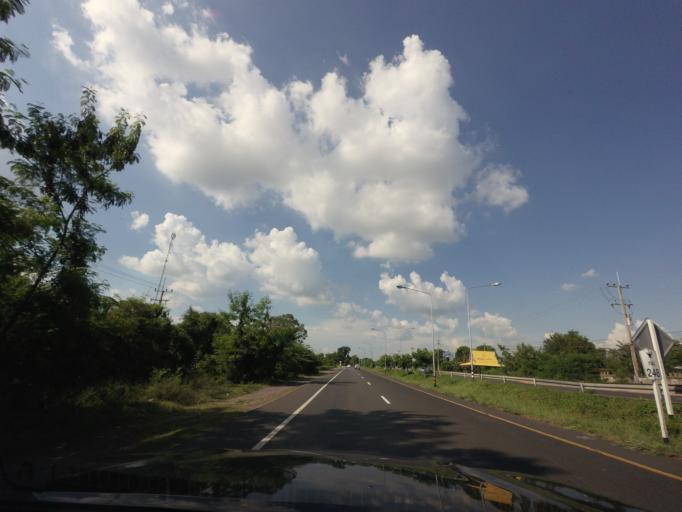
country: TH
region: Nakhon Ratchasima
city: Bua Lai
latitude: 15.6805
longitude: 102.5770
